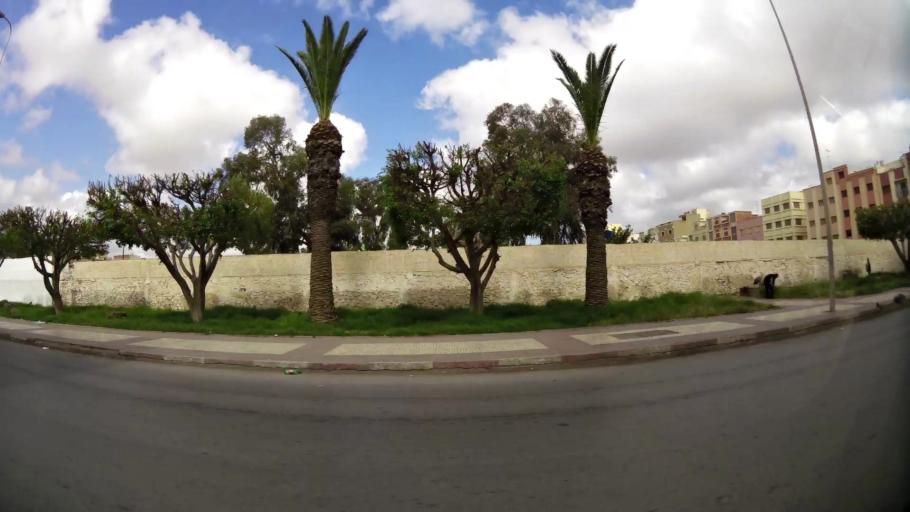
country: MA
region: Oriental
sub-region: Nador
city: Nador
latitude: 35.1699
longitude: -2.9253
